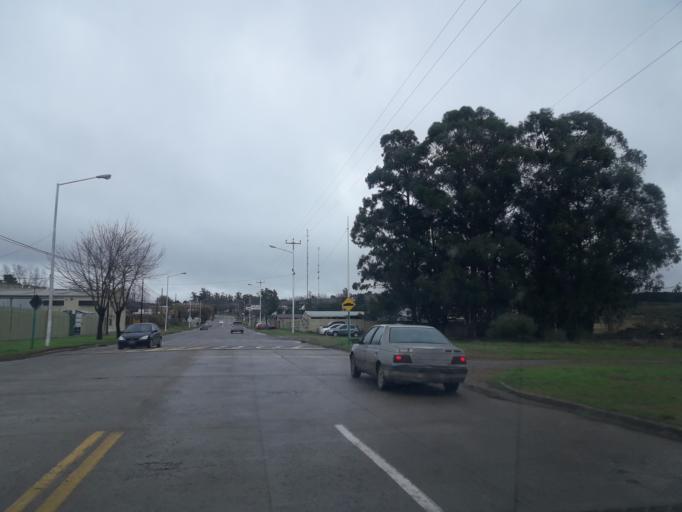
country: AR
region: Buenos Aires
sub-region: Partido de Tandil
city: Tandil
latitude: -37.3220
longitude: -59.1664
